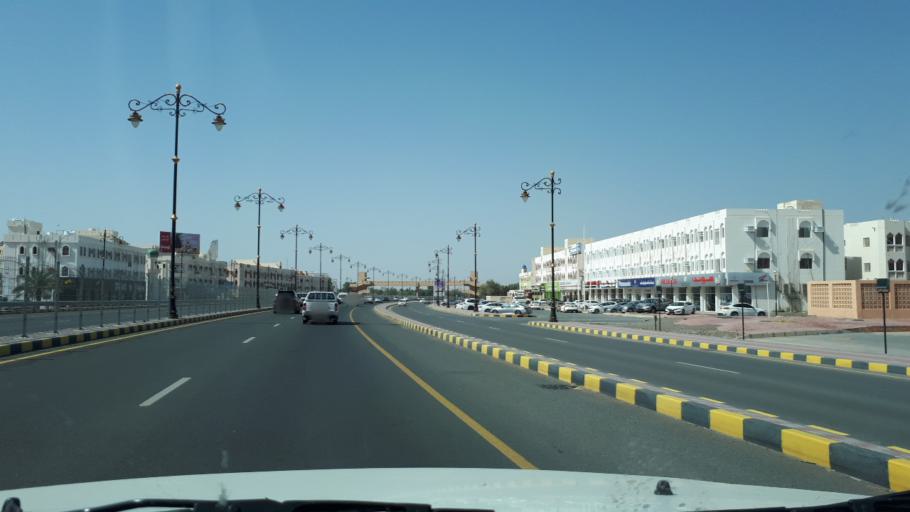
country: OM
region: Muhafazat ad Dakhiliyah
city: Nizwa
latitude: 22.8949
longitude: 57.5312
